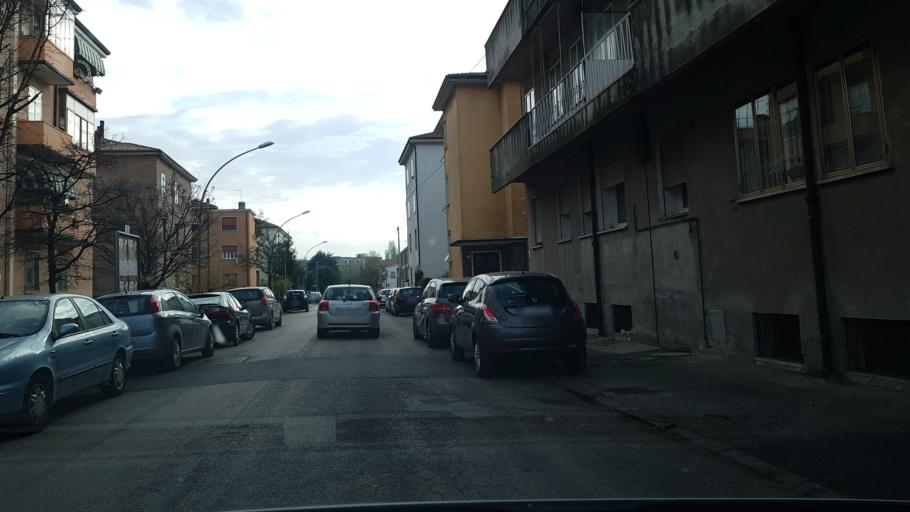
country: IT
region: Veneto
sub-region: Provincia di Rovigo
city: Rovigo
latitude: 45.0781
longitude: 11.7876
